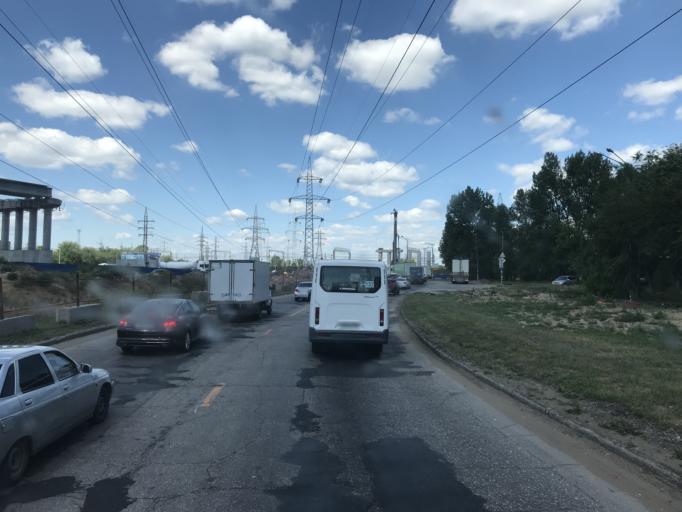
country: RU
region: Samara
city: Zhigulevsk
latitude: 53.4781
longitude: 49.5120
